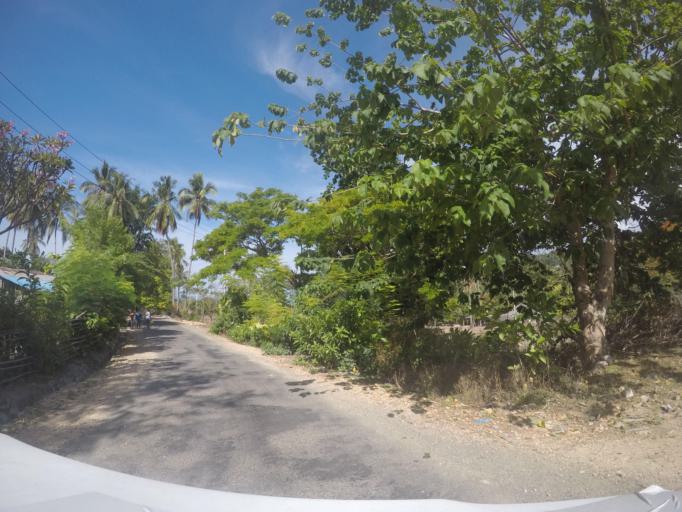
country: TL
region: Baucau
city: Baucau
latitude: -8.4574
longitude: 126.4585
